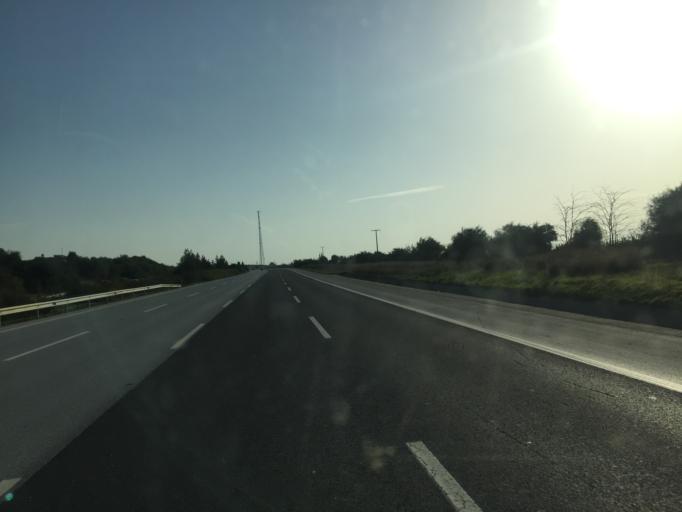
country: TR
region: Mersin
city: Yenice
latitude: 37.0230
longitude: 35.0767
